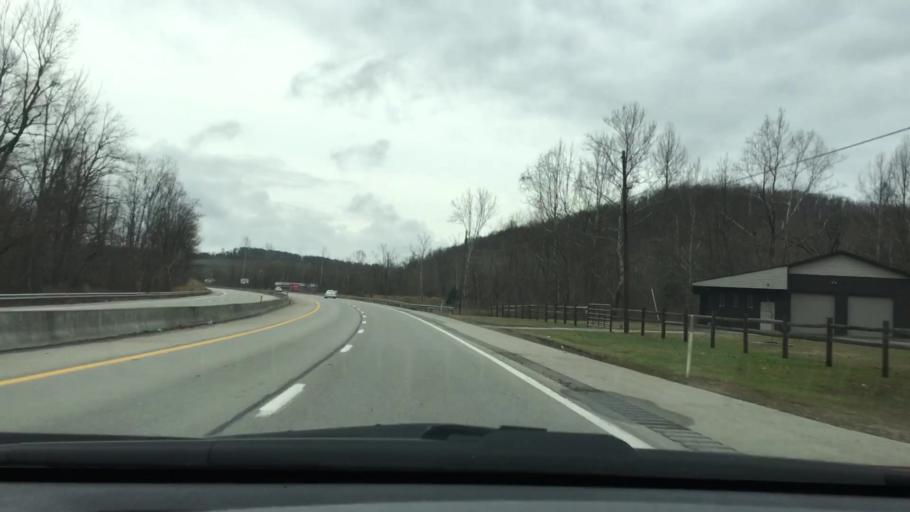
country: US
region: Pennsylvania
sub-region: Fayette County
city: Oliver
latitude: 39.9891
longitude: -79.7659
